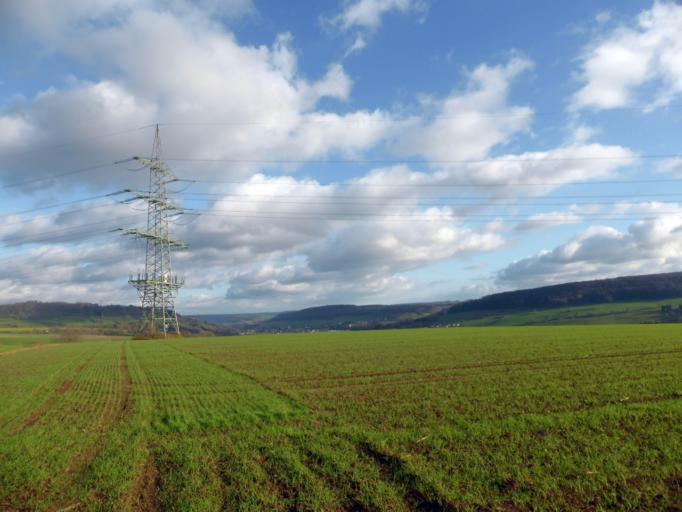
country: LU
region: Diekirch
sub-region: Canton de Diekirch
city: Erpeldange
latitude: 49.8684
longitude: 6.1288
